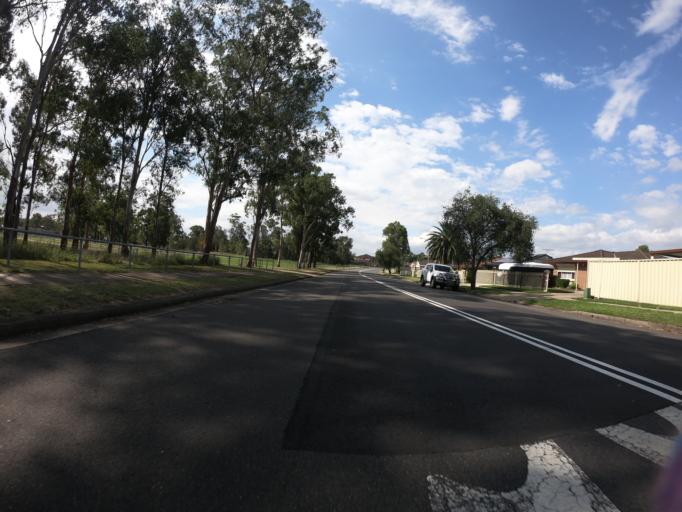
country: AU
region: New South Wales
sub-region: Blacktown
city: Hassall Grove
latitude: -33.7384
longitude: 150.8360
